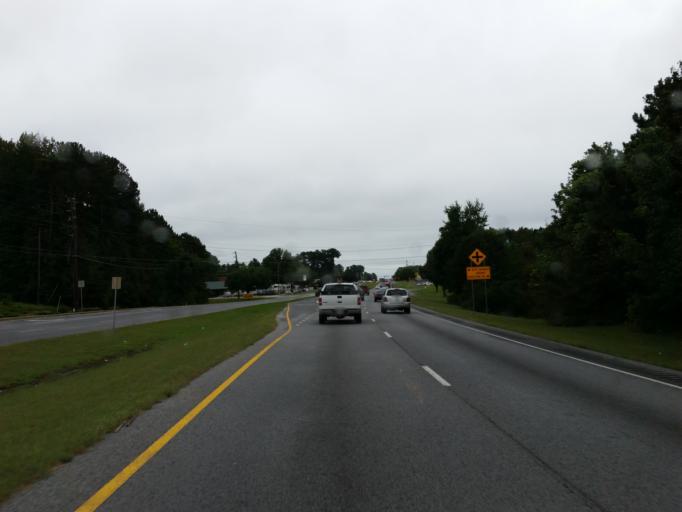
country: US
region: Georgia
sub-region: Clayton County
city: Irondale
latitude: 33.4938
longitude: -84.3427
